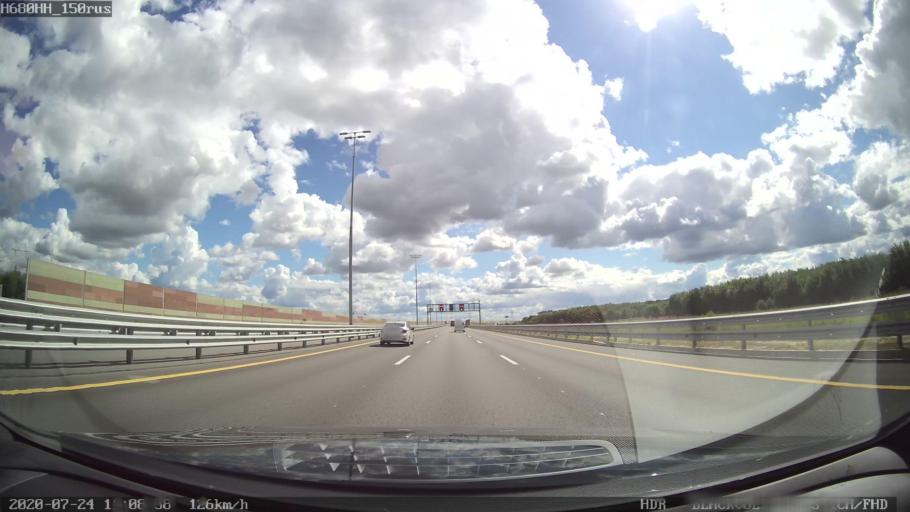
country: RU
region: St.-Petersburg
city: Tyarlevo
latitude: 59.7515
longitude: 30.4558
